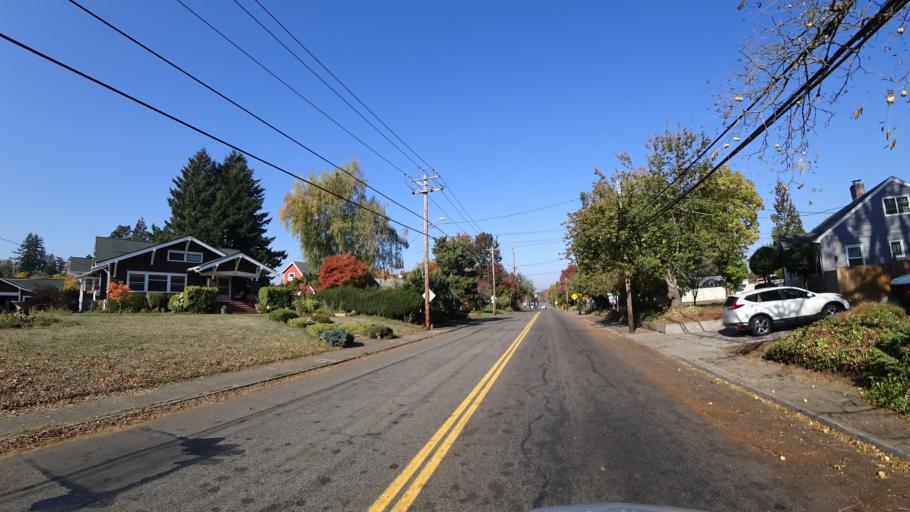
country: US
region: Oregon
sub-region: Multnomah County
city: Gresham
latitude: 45.4940
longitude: -122.4268
